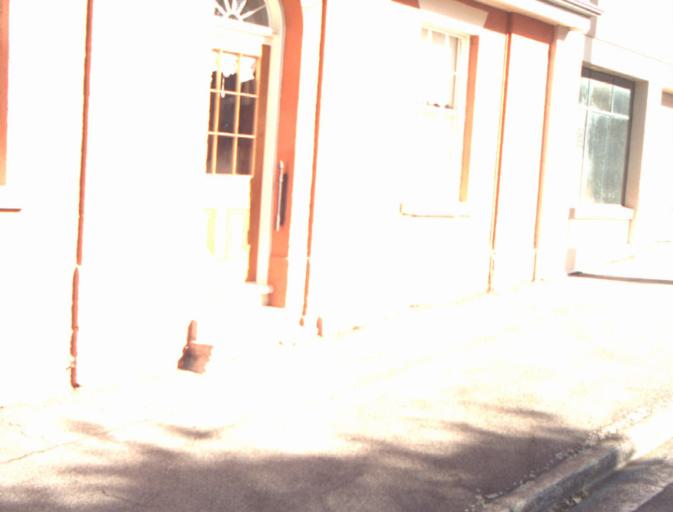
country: AU
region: Tasmania
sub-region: Launceston
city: Launceston
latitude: -41.4446
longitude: 147.1357
